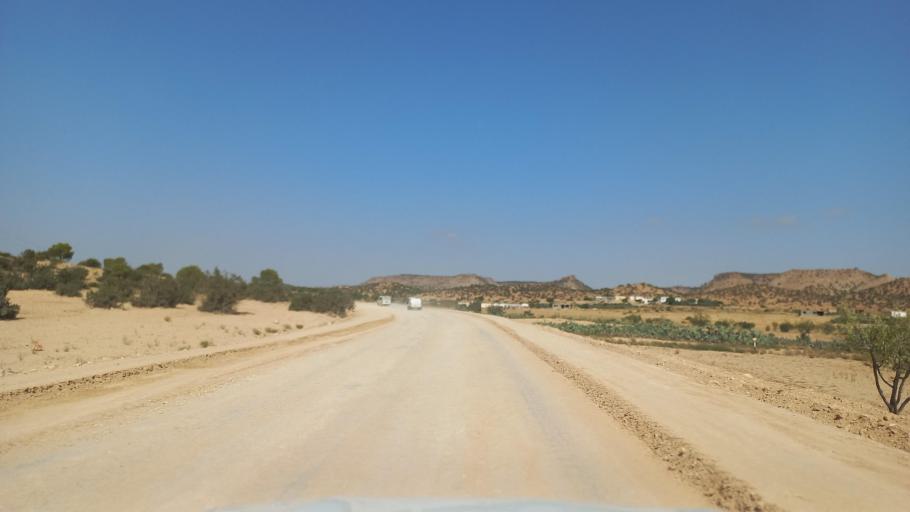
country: TN
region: Al Qasrayn
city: Sbiba
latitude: 35.4038
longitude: 8.9961
